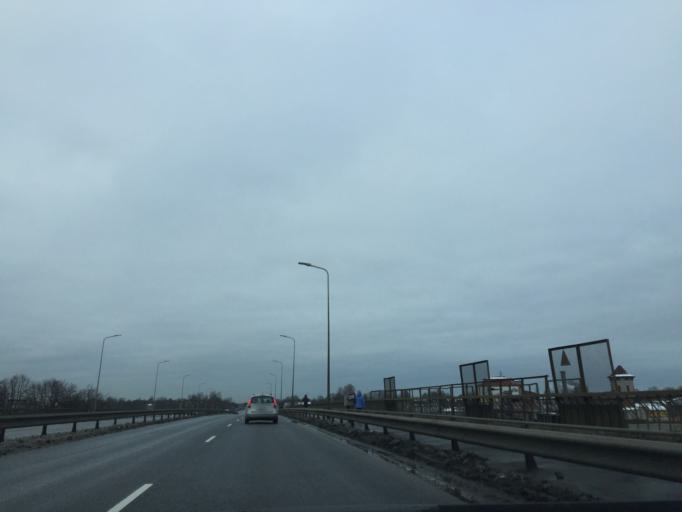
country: LV
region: Riga
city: Jaunciems
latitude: 56.9790
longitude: 24.1633
